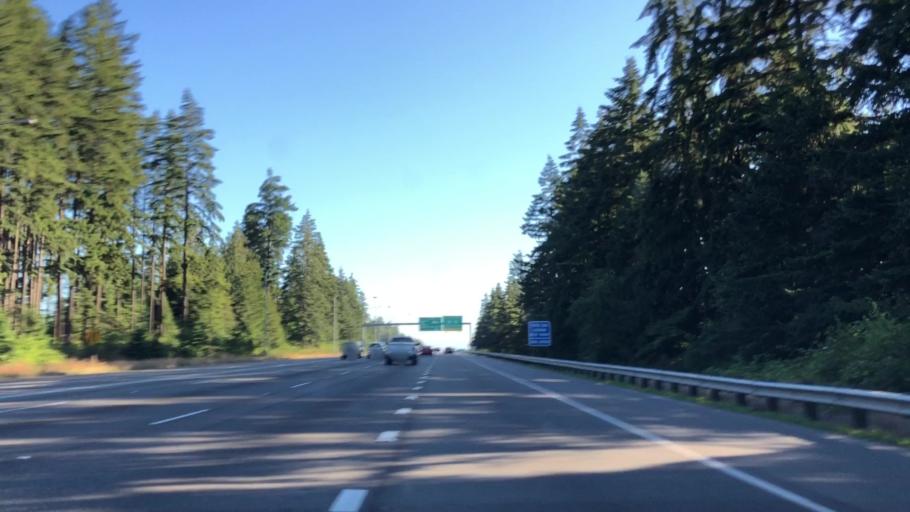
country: US
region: Washington
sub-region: Snohomish County
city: Mill Creek
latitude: 47.9044
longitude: -122.2115
